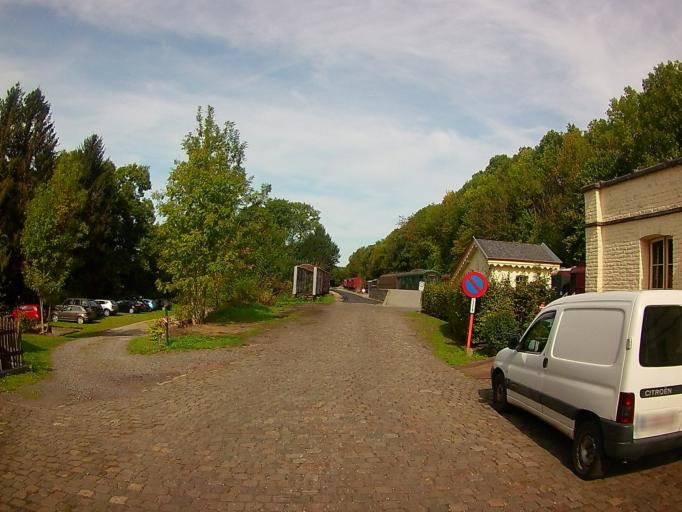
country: BE
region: Wallonia
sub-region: Province de Liege
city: Plombieres
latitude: 50.7230
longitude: 5.9129
